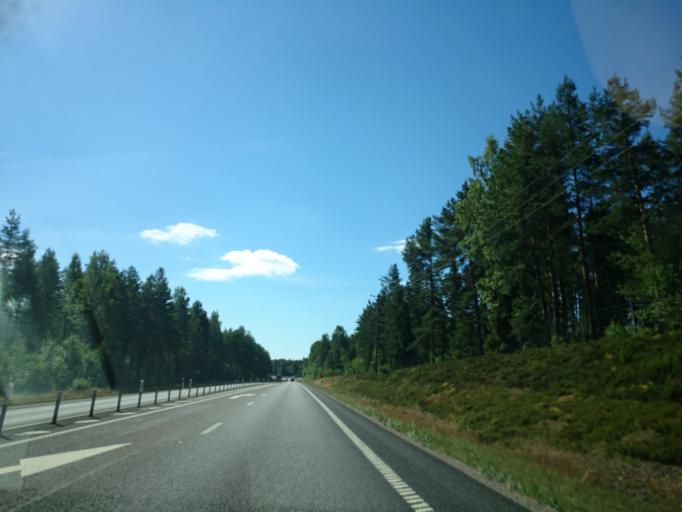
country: SE
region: Gaevleborg
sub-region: Gavle Kommun
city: Norrsundet
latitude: 61.0122
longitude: 16.9814
